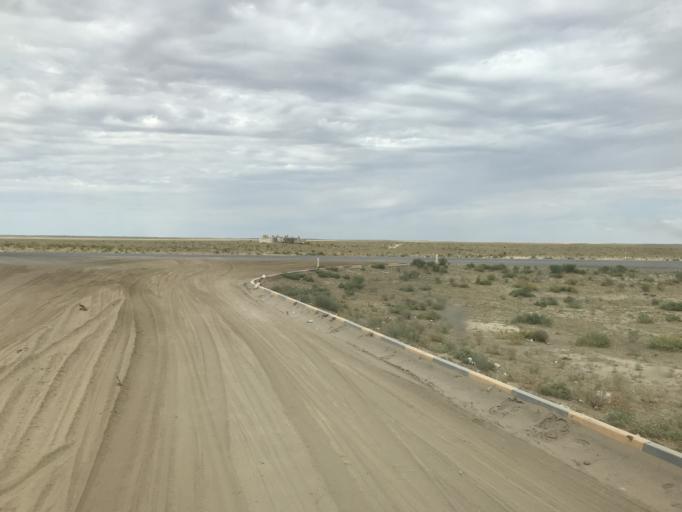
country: KZ
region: Qyzylorda
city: Aral
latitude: 46.8290
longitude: 61.6918
